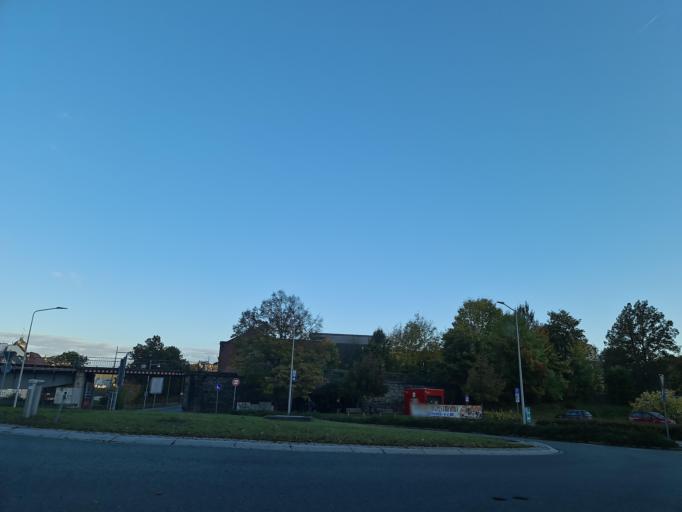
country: DE
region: Thuringia
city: Greiz
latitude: 50.6563
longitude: 12.1949
